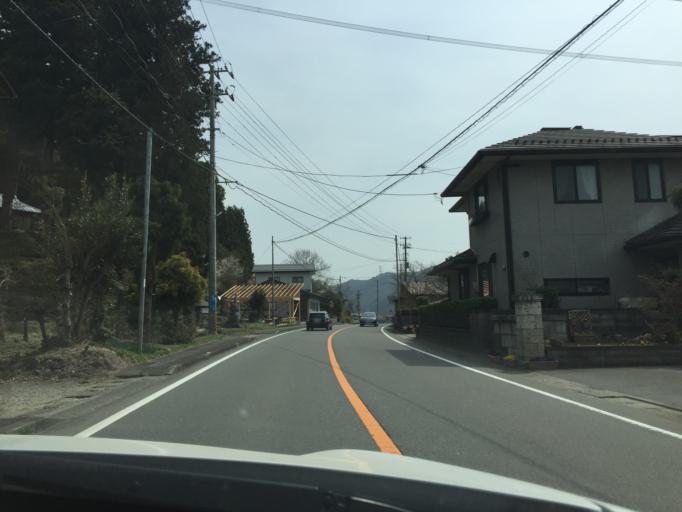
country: JP
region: Fukushima
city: Ishikawa
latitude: 37.1181
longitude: 140.5044
